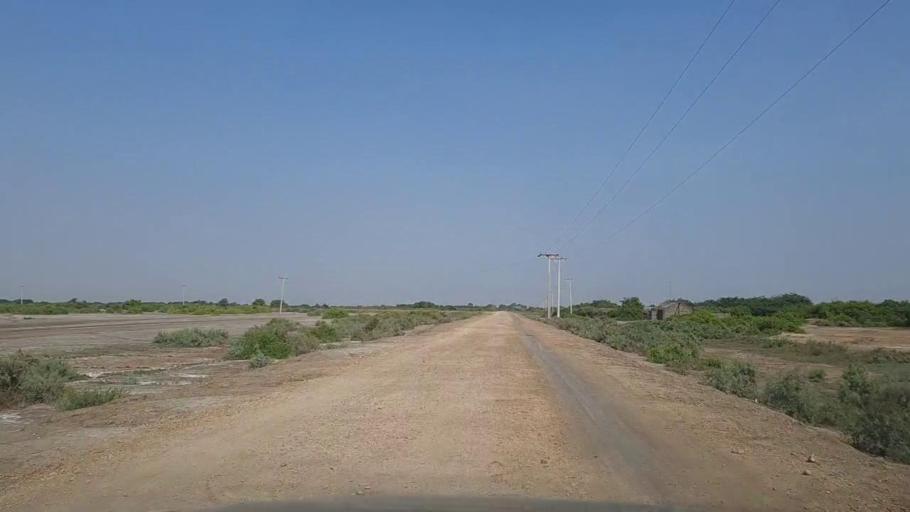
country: PK
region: Sindh
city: Thatta
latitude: 24.6057
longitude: 67.9546
